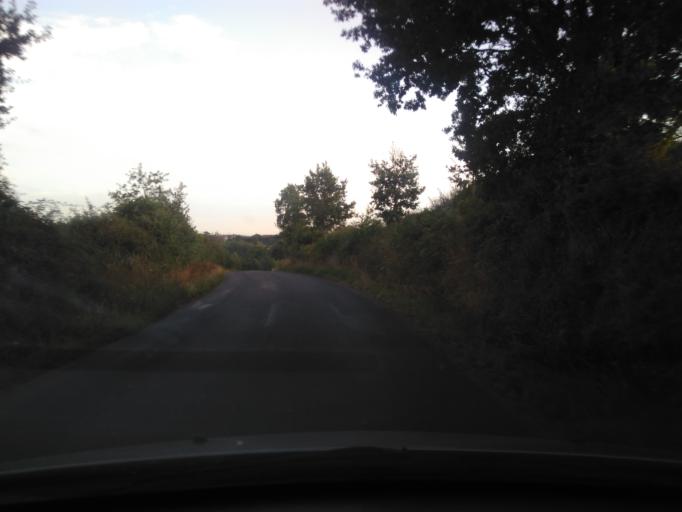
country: FR
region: Pays de la Loire
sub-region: Departement de la Vendee
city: Nesmy
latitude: 46.5958
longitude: -1.3624
